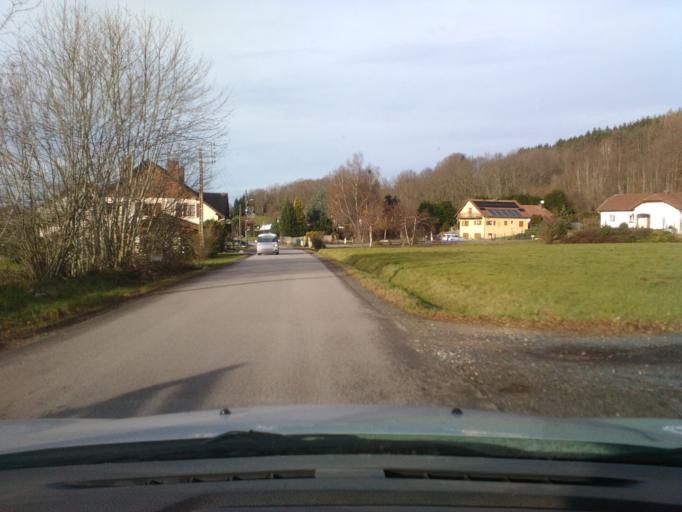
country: FR
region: Lorraine
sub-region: Departement des Vosges
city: Fraize
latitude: 48.1745
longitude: 6.9786
